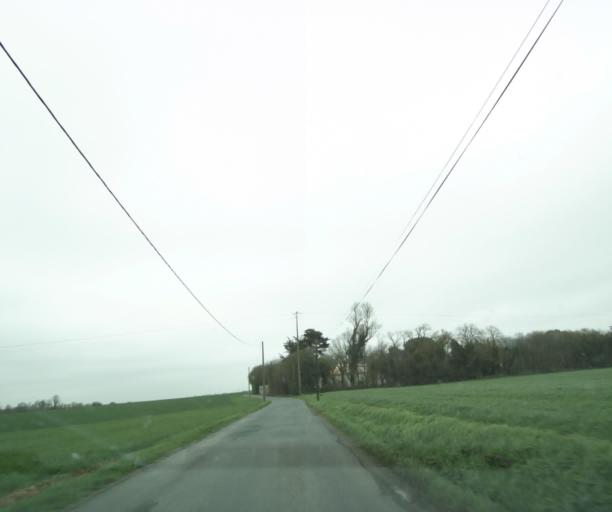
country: FR
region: Poitou-Charentes
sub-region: Departement de la Charente-Maritime
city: Puilboreau
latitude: 46.1858
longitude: -1.1357
